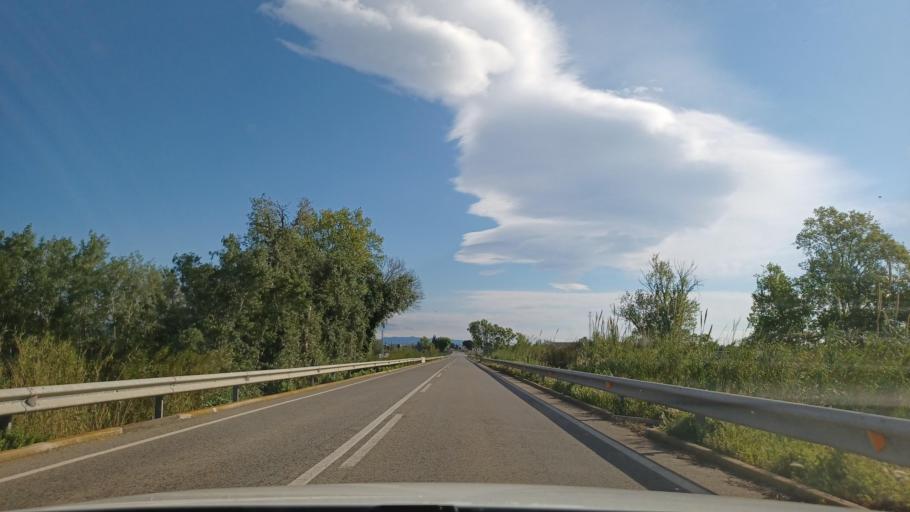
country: ES
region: Catalonia
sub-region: Provincia de Tarragona
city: Amposta
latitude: 40.7166
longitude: 0.5835
